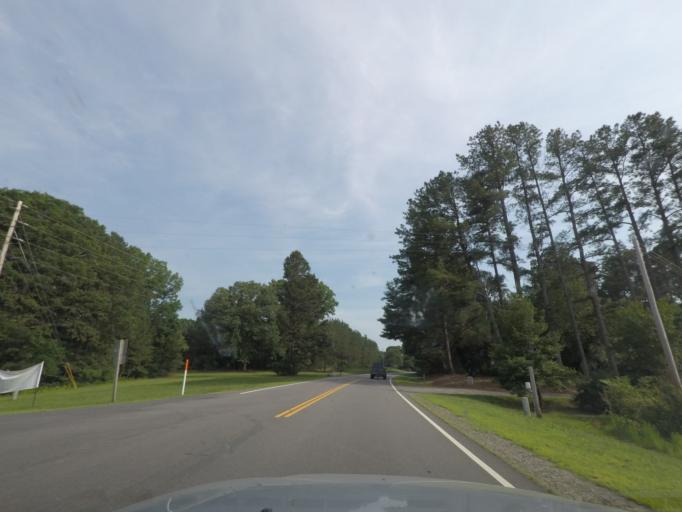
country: US
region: Virginia
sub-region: Mecklenburg County
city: Chase City
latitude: 36.7986
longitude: -78.6043
